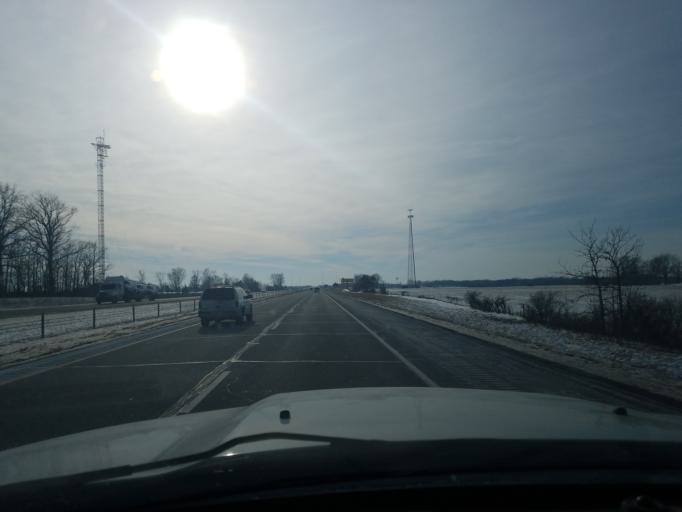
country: US
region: Indiana
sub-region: Huntington County
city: Warren
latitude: 40.7293
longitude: -85.4252
